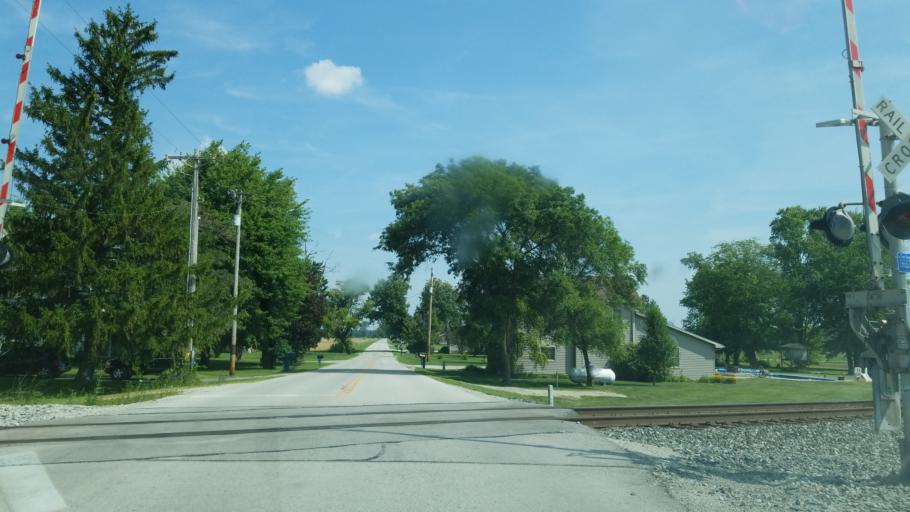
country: US
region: Ohio
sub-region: Seneca County
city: Fostoria
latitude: 41.1850
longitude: -83.3185
